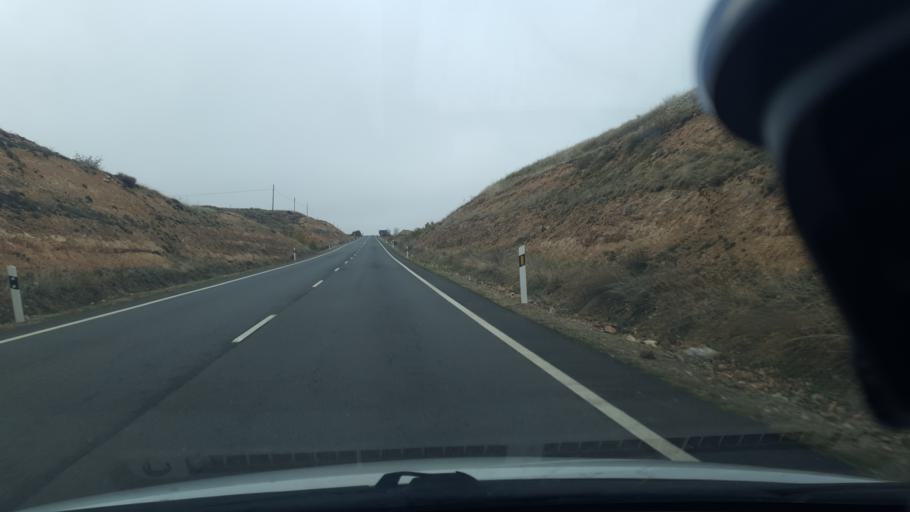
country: ES
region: Castille and Leon
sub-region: Provincia de Segovia
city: Encinillas
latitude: 41.0123
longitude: -4.1457
